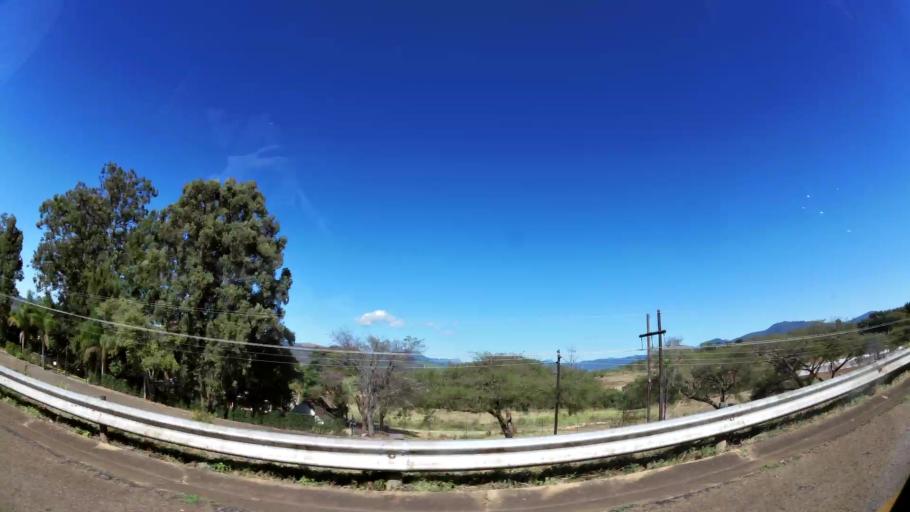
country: ZA
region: Limpopo
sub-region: Mopani District Municipality
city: Tzaneen
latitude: -23.8388
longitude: 30.1382
